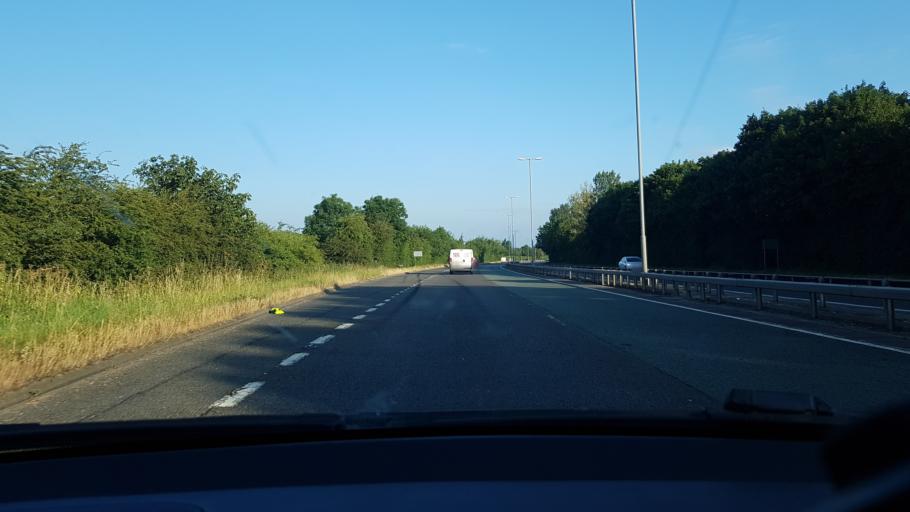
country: GB
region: England
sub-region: Nottinghamshire
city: Eastwood
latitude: 53.0053
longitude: -1.3052
